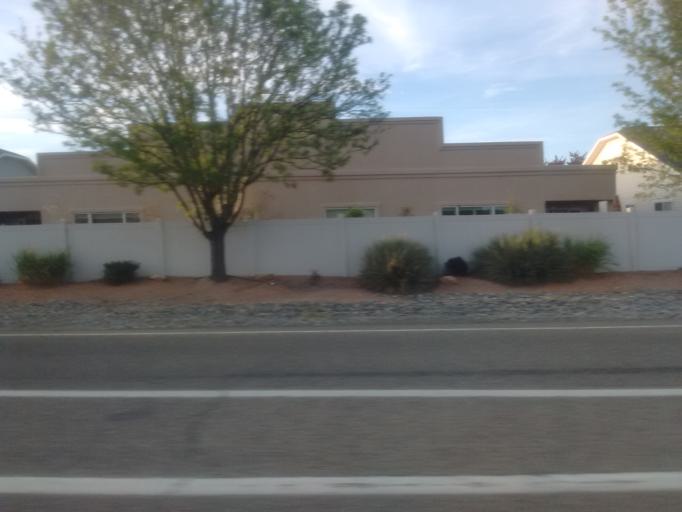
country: US
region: Colorado
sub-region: Mesa County
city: Redlands
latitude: 39.1063
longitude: -108.6010
